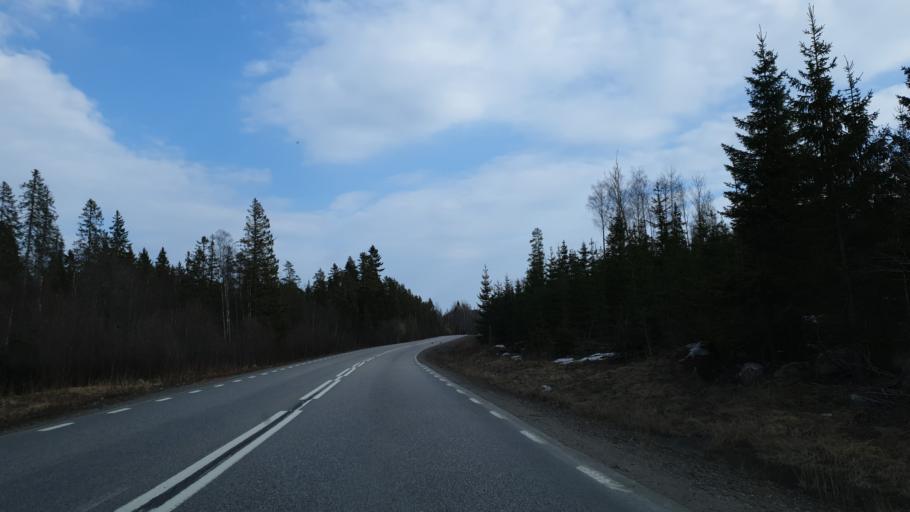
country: SE
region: Gaevleborg
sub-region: Hudiksvalls Kommun
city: Iggesund
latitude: 61.6530
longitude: 17.0260
